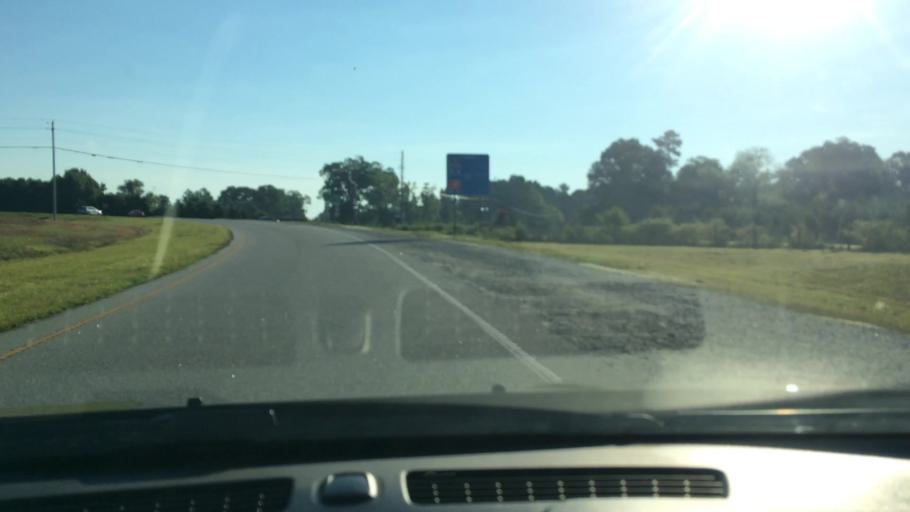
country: US
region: North Carolina
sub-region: Pitt County
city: Summerfield
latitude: 35.6274
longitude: -77.4330
